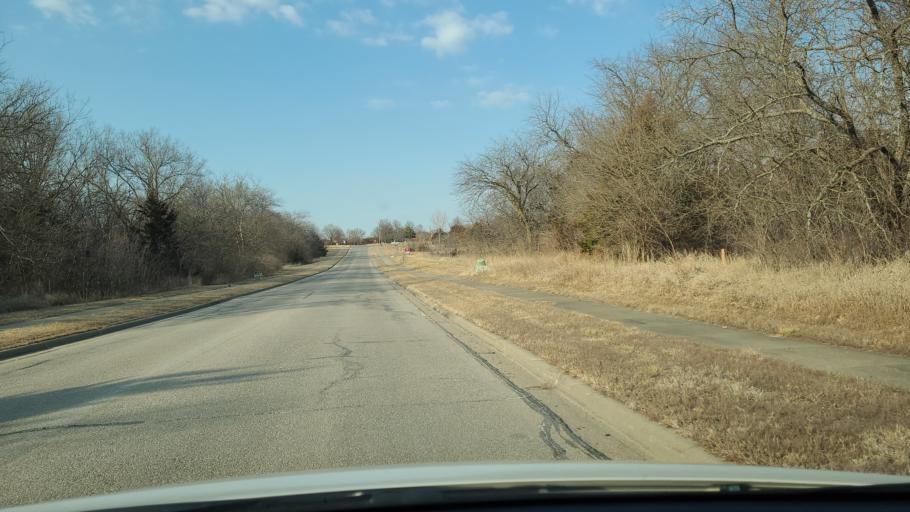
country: US
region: Kansas
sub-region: Douglas County
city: Lawrence
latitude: 38.9540
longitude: -95.3106
